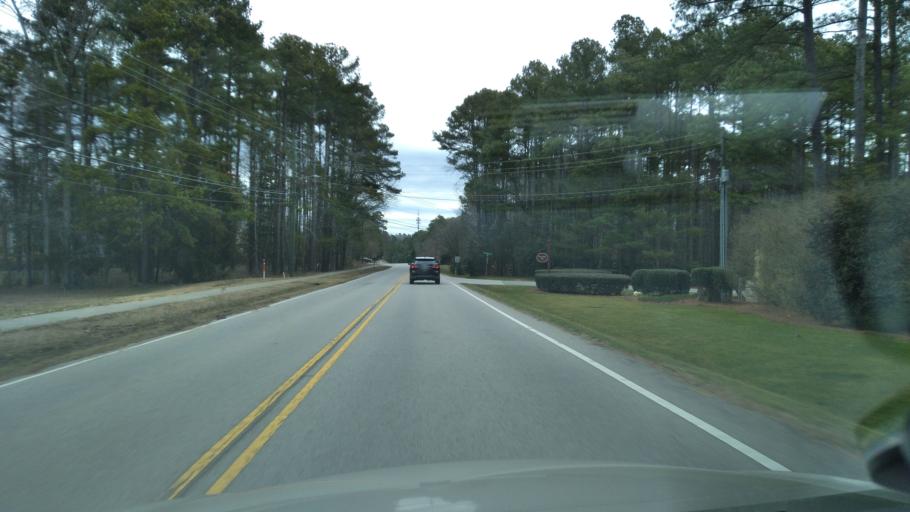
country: US
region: North Carolina
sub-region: Wake County
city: Apex
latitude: 35.7374
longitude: -78.8287
